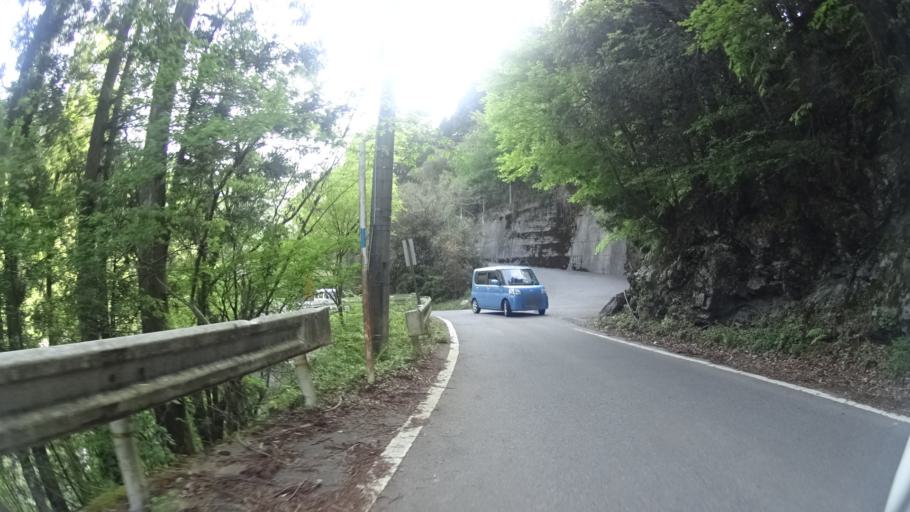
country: JP
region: Tokushima
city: Ikedacho
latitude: 33.8658
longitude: 133.9599
